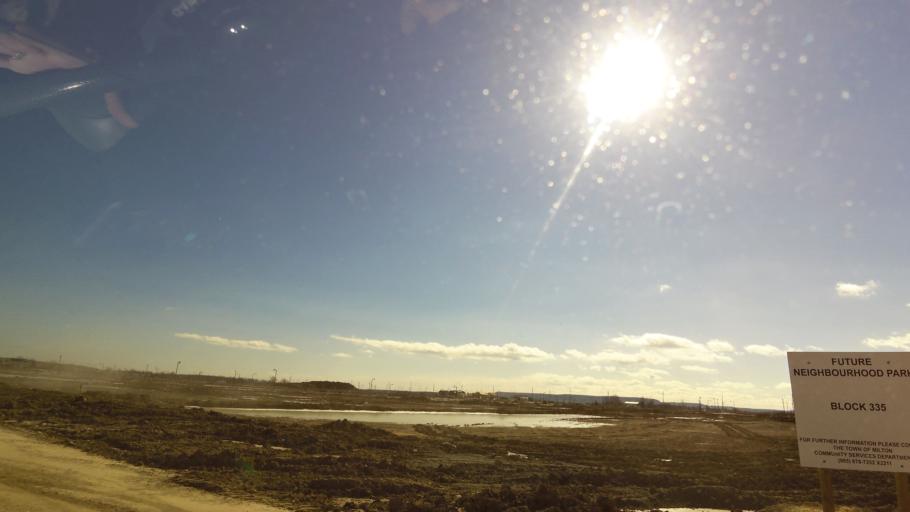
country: CA
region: Ontario
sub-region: Halton
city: Milton
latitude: 43.4841
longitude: -79.8475
